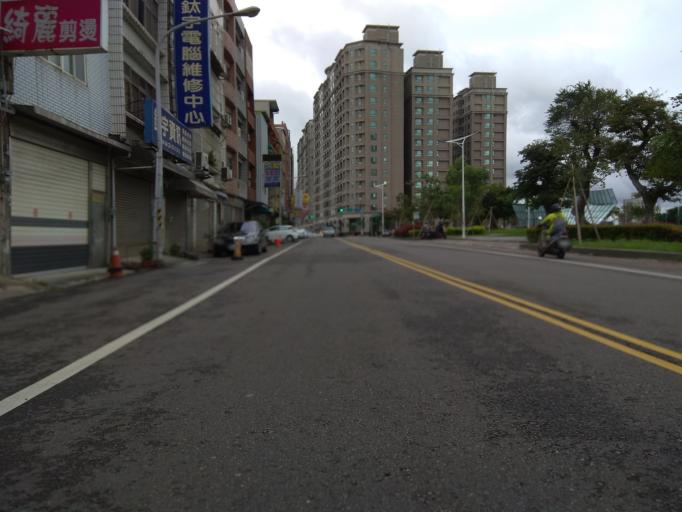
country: TW
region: Taiwan
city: Taoyuan City
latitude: 24.9612
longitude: 121.2178
